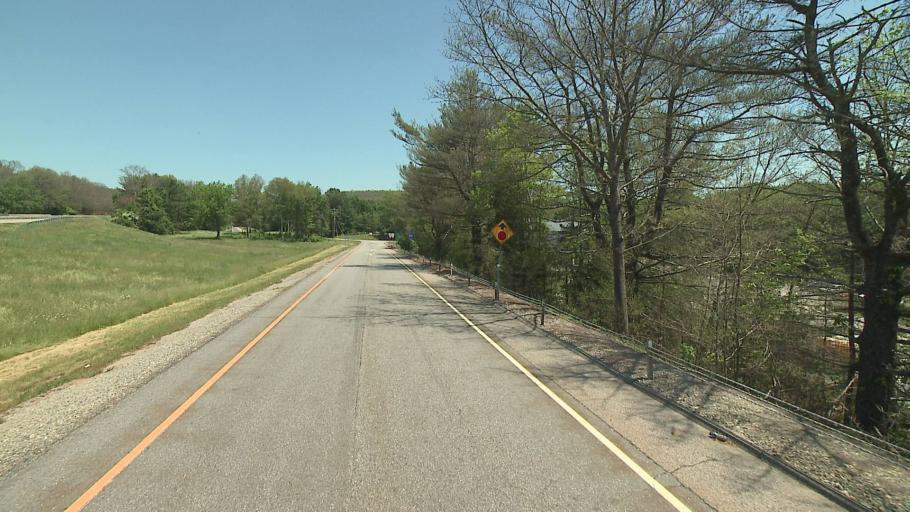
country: US
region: Connecticut
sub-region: Windham County
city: Plainfield
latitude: 41.6828
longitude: -71.9076
